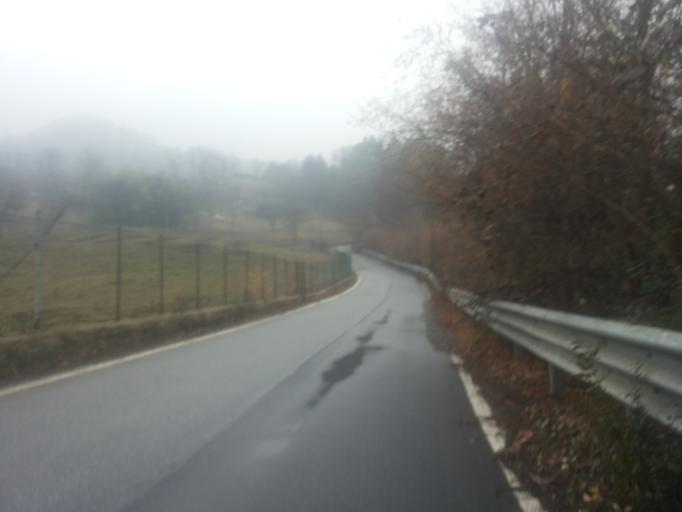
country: IT
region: Piedmont
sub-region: Provincia di Torino
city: Revigliasco
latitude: 45.0478
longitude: 7.7221
